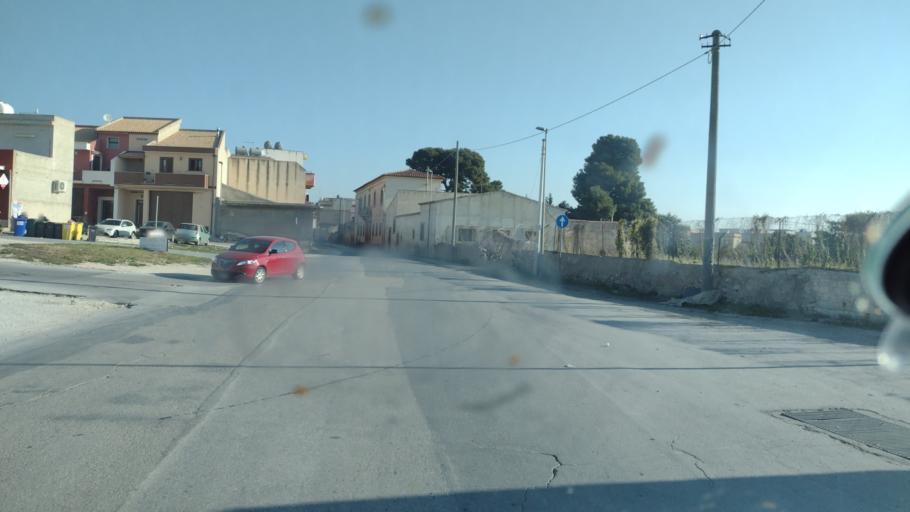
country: IT
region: Sicily
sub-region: Provincia di Siracusa
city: Avola
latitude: 36.9009
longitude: 15.1353
